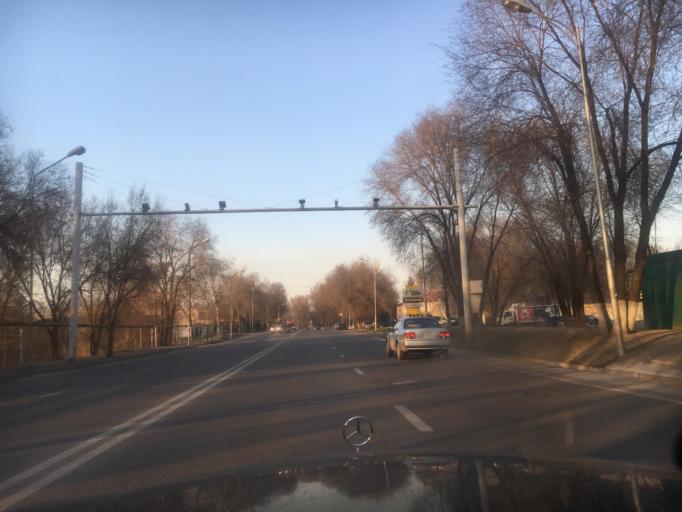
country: KZ
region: Almaty Oblysy
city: Pervomayskiy
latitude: 43.3645
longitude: 76.9845
